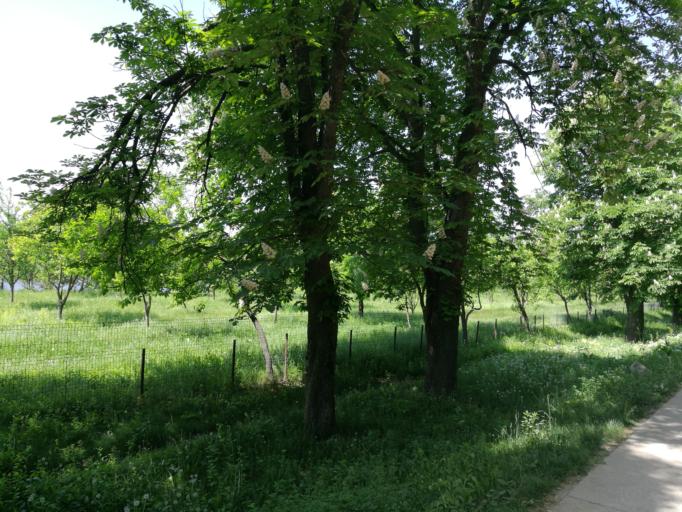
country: RO
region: Ilfov
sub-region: Comuna Gradistea
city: Gradistea
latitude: 44.6763
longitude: 26.2659
